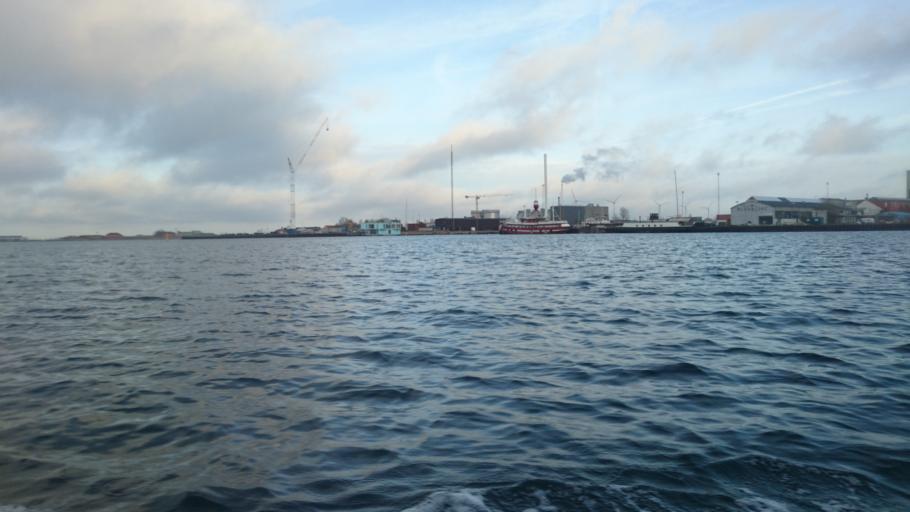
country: DK
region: Capital Region
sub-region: Kobenhavn
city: Christianshavn
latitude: 55.6930
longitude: 12.6035
